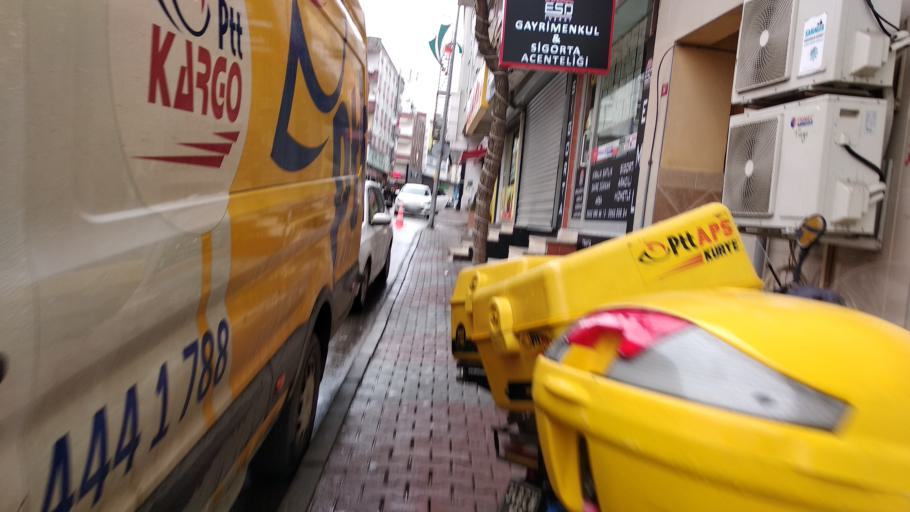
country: TR
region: Istanbul
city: Samandira
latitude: 41.0161
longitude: 29.1902
